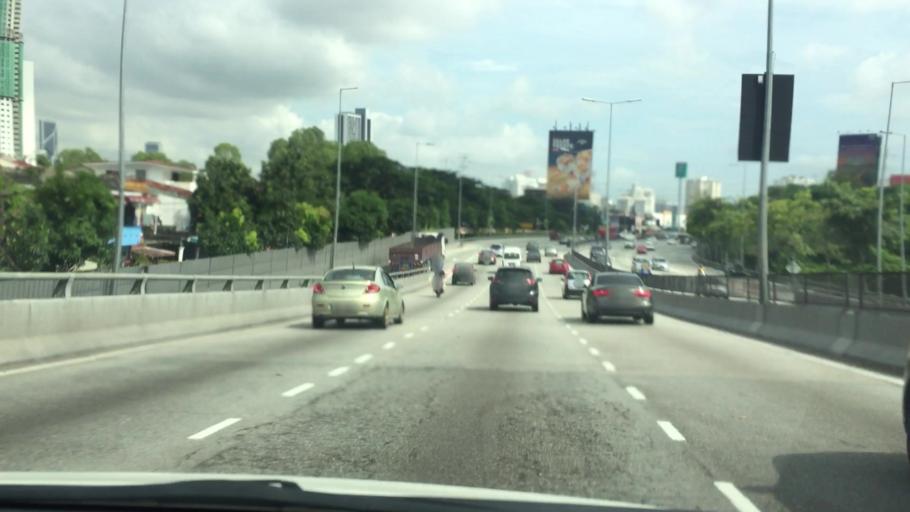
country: MY
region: Kuala Lumpur
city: Kuala Lumpur
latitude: 3.1382
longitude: 101.7435
